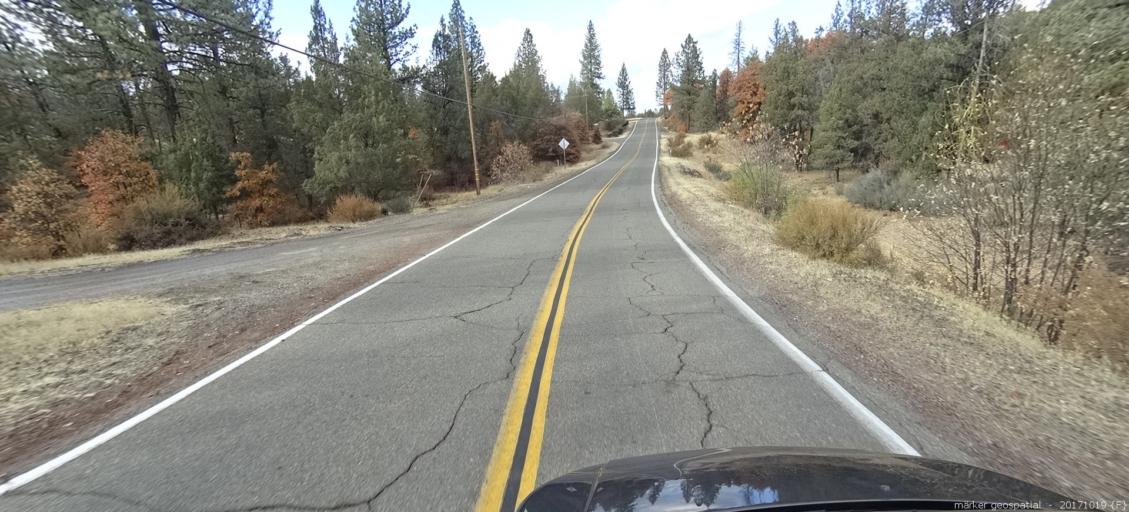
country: US
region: California
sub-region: Shasta County
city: Burney
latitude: 40.9770
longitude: -121.4334
